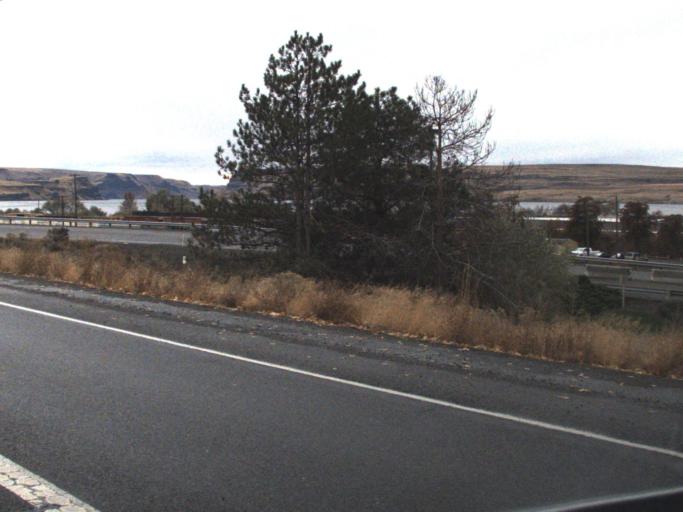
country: US
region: Washington
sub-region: Benton County
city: Finley
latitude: 46.1006
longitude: -118.9127
